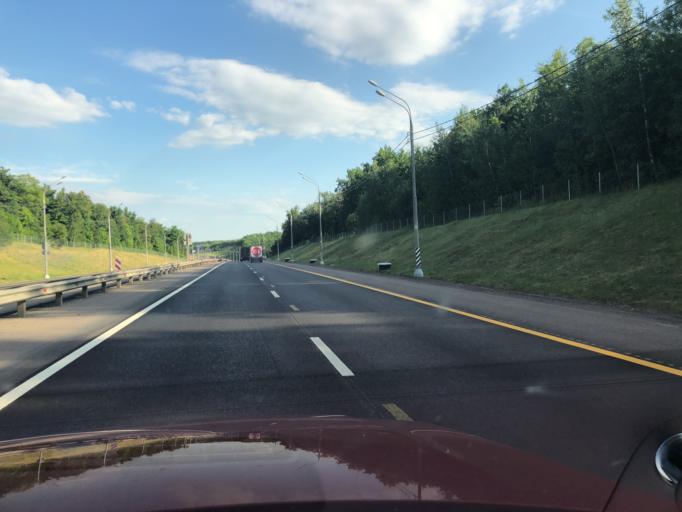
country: RU
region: Lipetsk
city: Zadonsk
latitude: 52.3976
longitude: 38.8605
